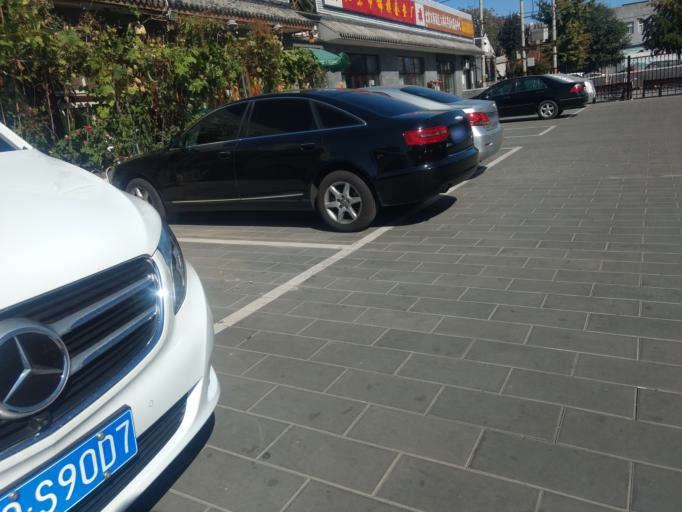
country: CN
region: Beijing
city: Beijing
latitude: 39.8885
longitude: 116.3820
